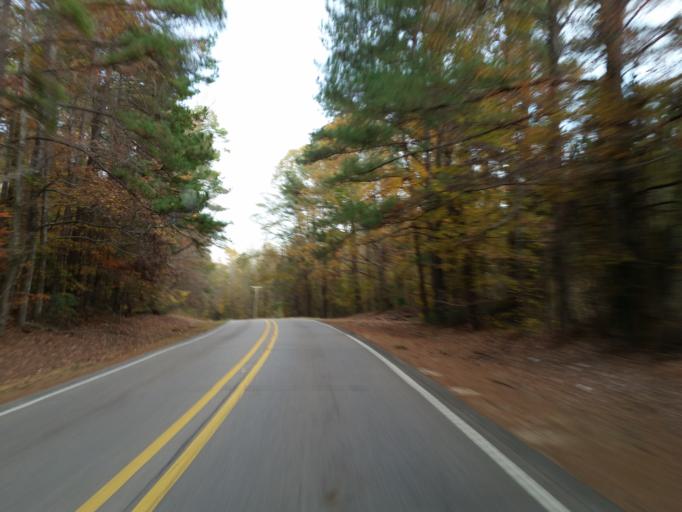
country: US
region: Mississippi
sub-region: Lauderdale County
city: Marion
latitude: 32.4100
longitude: -88.5629
